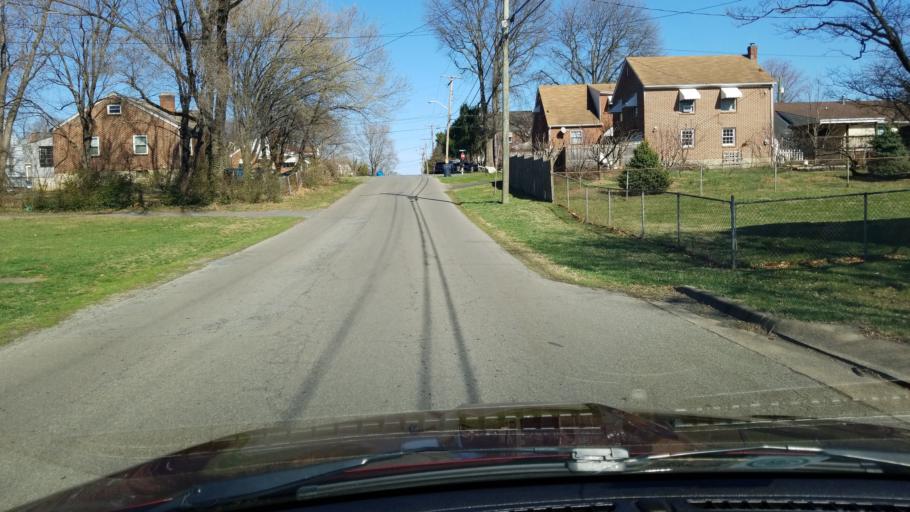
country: US
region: Virginia
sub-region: City of Roanoke
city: Roanoke
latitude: 37.3001
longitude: -79.9364
